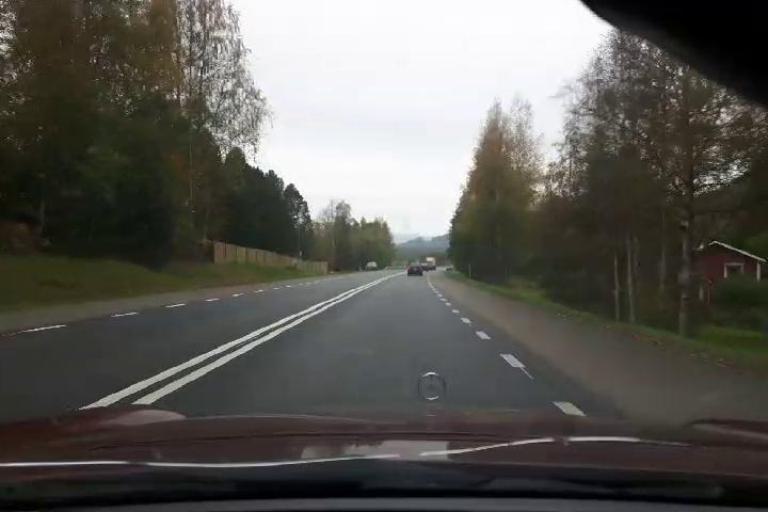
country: SE
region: Vaesternorrland
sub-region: OErnskoeldsviks Kommun
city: Ornskoldsvik
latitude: 63.2962
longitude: 18.6663
